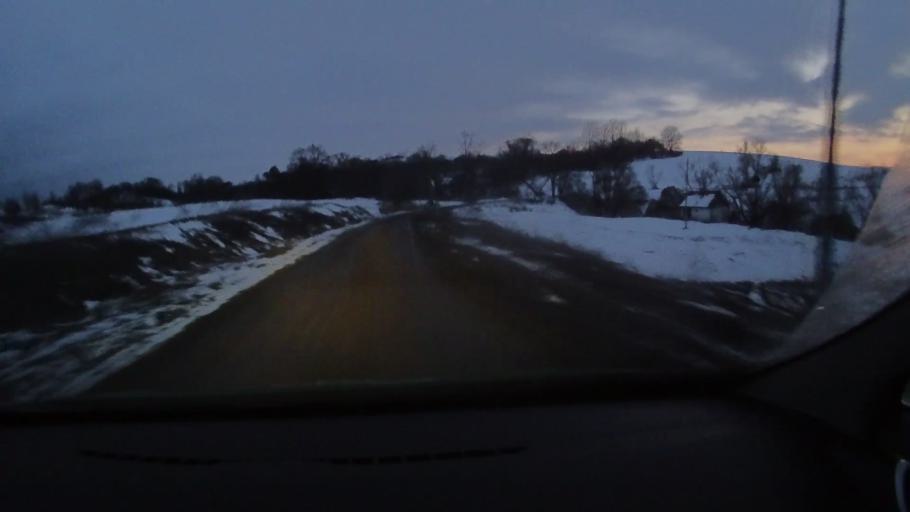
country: RO
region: Harghita
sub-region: Comuna Darjiu
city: Darjiu
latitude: 46.1684
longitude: 25.2273
